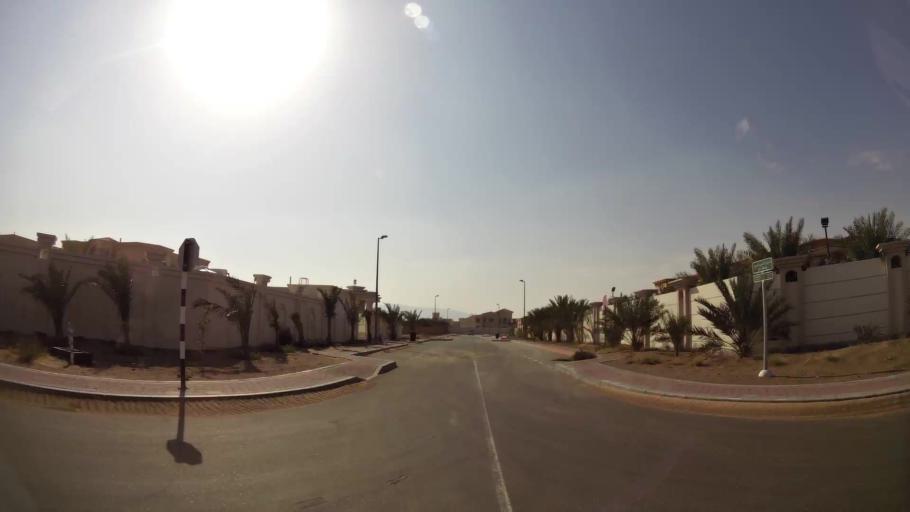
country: AE
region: Abu Dhabi
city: Al Ain
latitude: 24.0865
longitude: 55.9032
